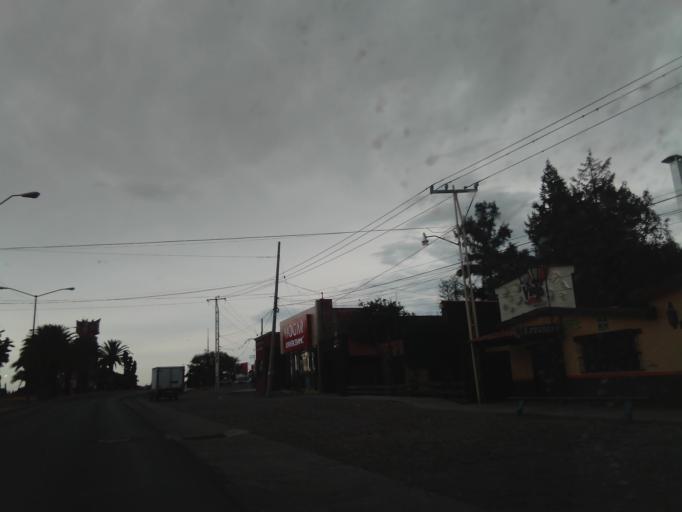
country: MX
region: Guanajuato
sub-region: Dolores Hidalgo Cuna de la Independencia Nacional
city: Dolores Hidalgo Cuna de la Independencia Nacional
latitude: 21.1575
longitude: -100.9185
